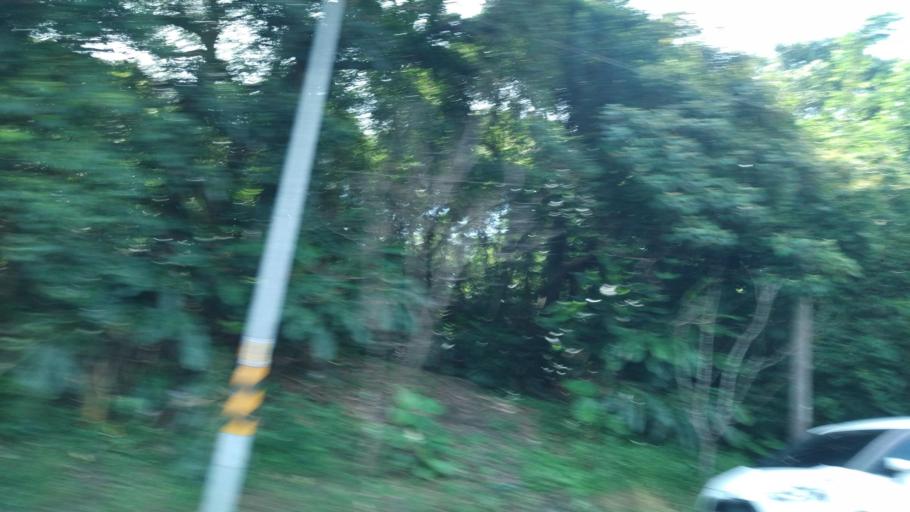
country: TW
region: Taipei
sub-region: Taipei
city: Banqiao
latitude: 24.9493
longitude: 121.5052
